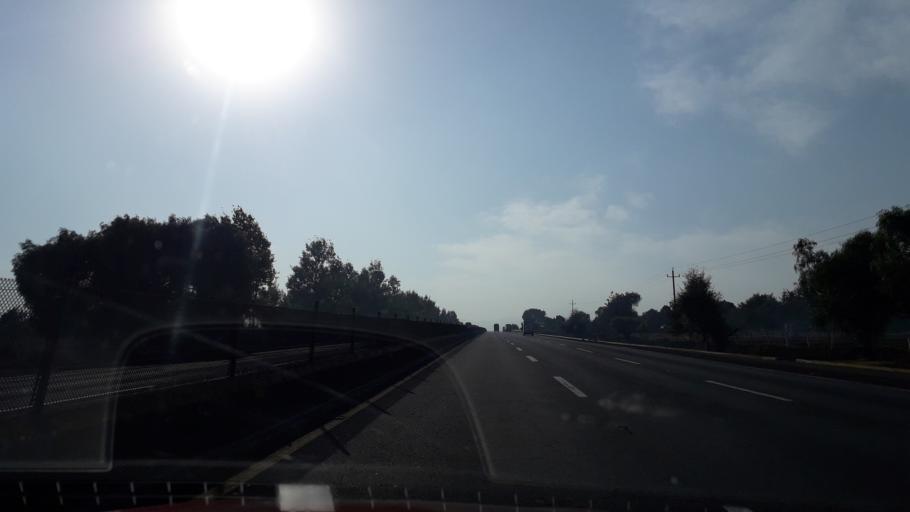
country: MX
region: Puebla
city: San Matias Tlalancaleca
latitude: 19.3266
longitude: -98.5308
